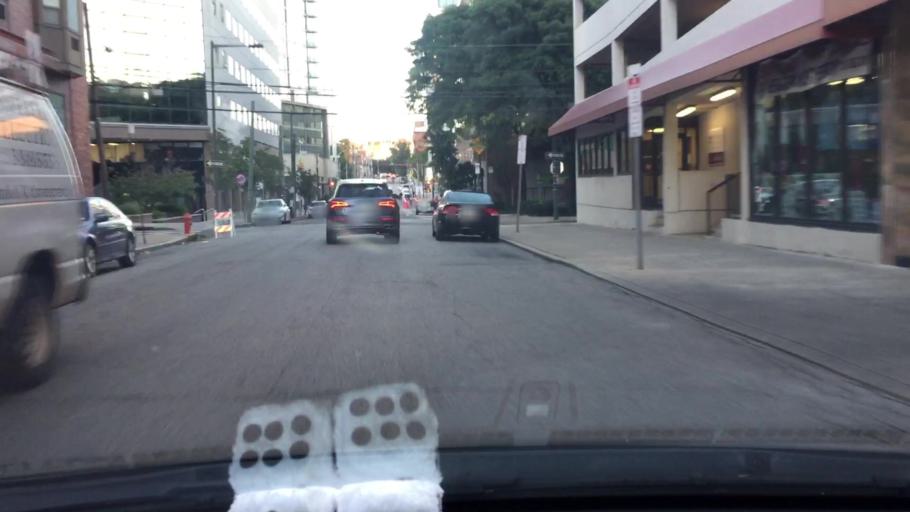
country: US
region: Pennsylvania
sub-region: Philadelphia County
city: Philadelphia
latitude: 39.9550
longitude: -75.1944
